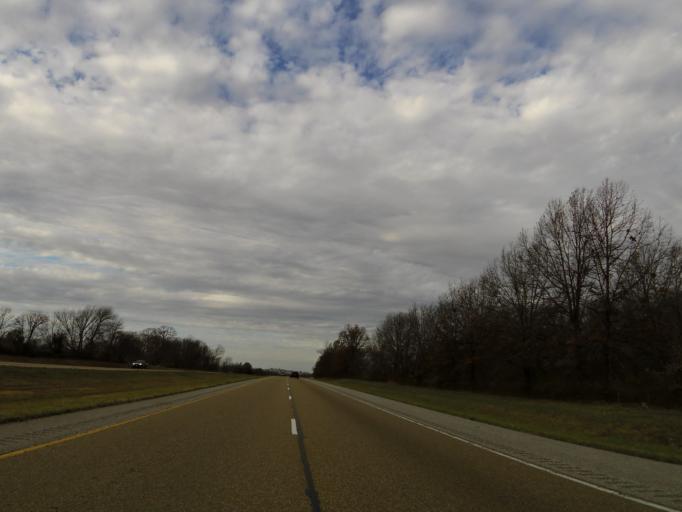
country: US
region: Illinois
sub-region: Clinton County
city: Wamac
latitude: 38.3893
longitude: -89.2099
